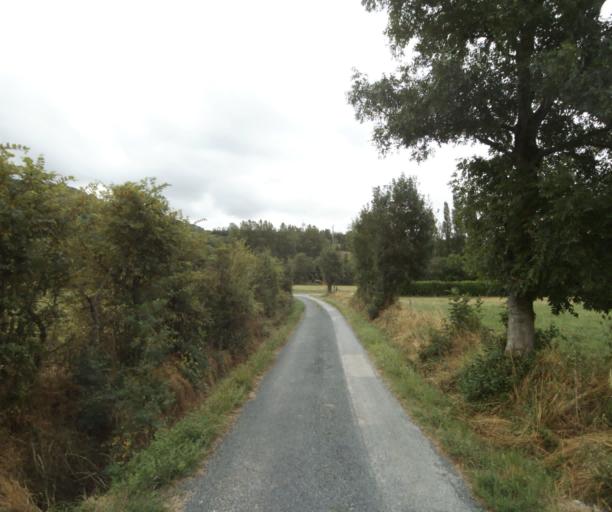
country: FR
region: Midi-Pyrenees
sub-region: Departement du Tarn
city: Soreze
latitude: 43.4454
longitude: 2.0573
